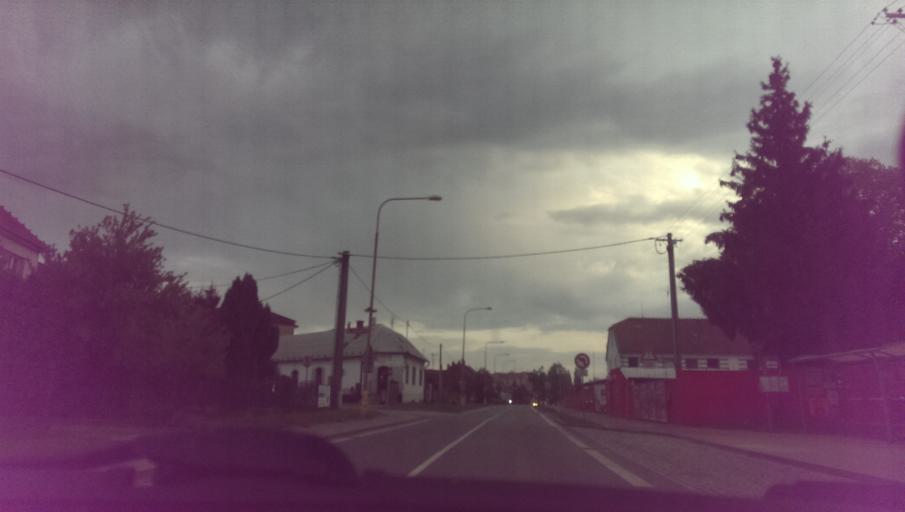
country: CZ
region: Zlin
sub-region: Okres Uherske Hradiste
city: Uherske Hradiste
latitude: 49.0725
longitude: 17.4799
